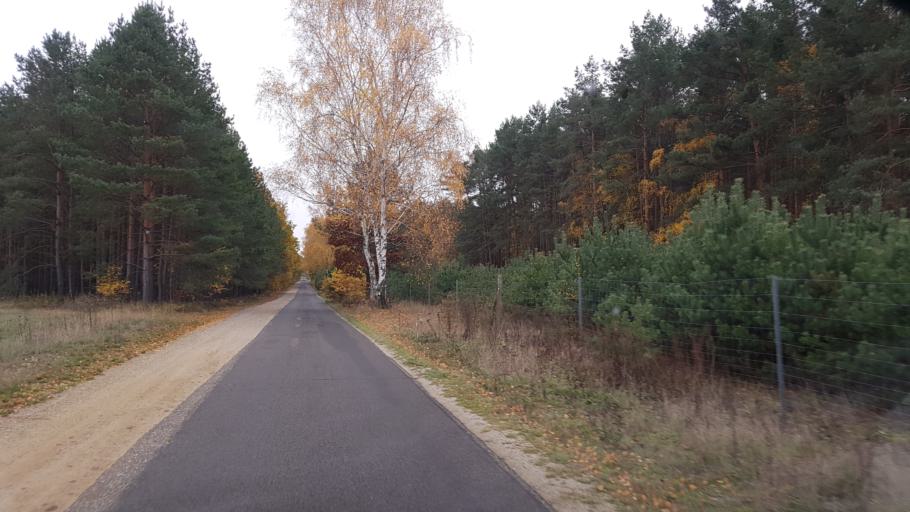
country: DE
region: Brandenburg
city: Crinitz
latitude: 51.7191
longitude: 13.7777
